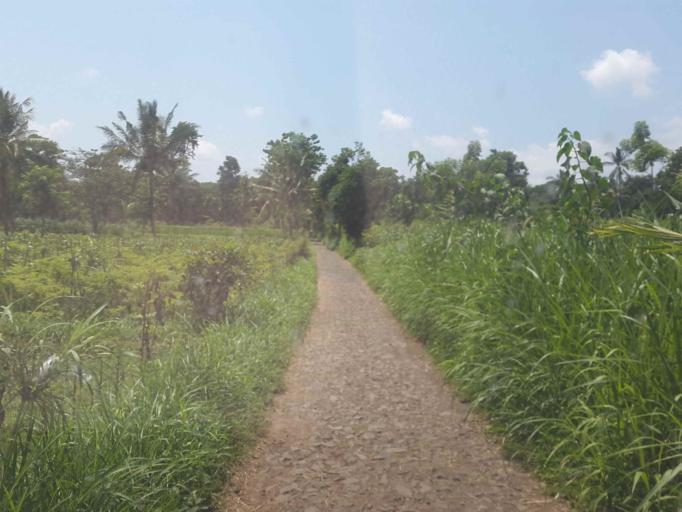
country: ID
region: East Java
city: Sumberpandan
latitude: -7.9695
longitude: 113.7805
